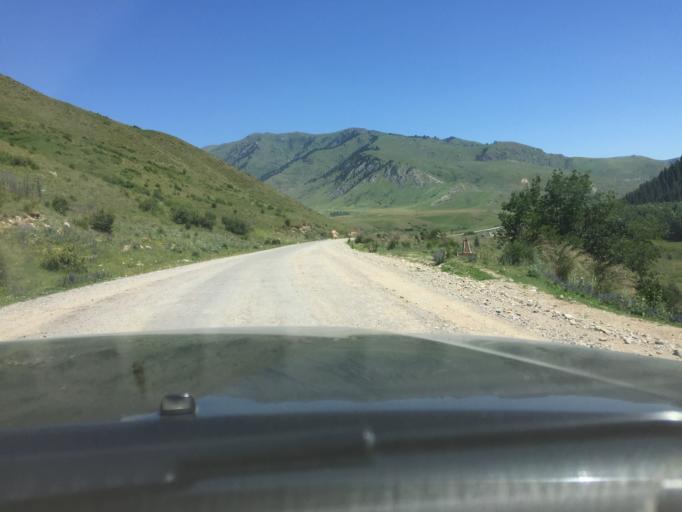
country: KG
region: Ysyk-Koel
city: Teploklyuchenka
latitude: 42.7297
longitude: 78.8229
